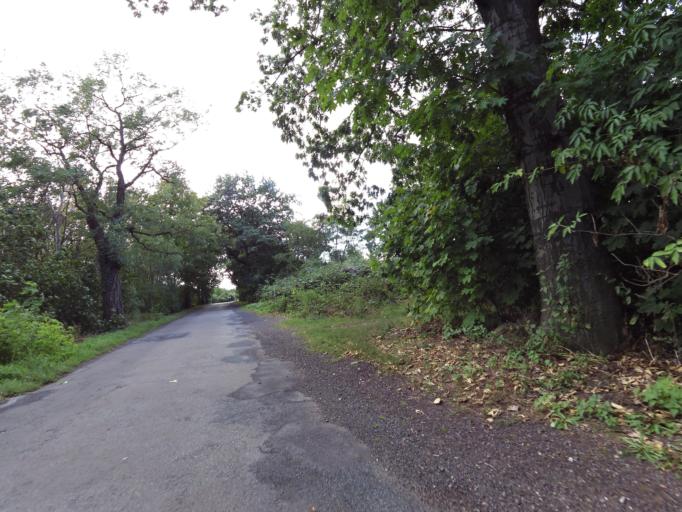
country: DE
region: Brandenburg
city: Grossbeeren
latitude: 52.3627
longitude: 13.3344
